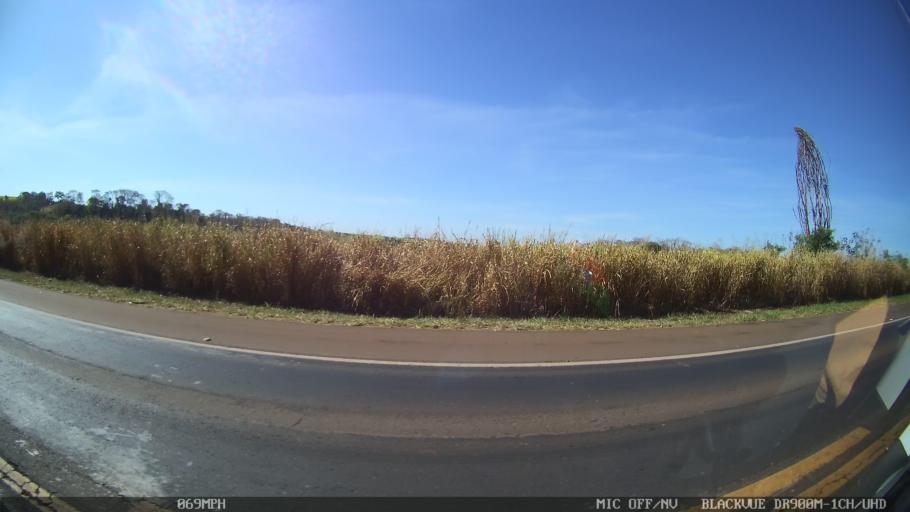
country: BR
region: Sao Paulo
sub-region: Olimpia
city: Olimpia
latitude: -20.7062
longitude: -48.8837
